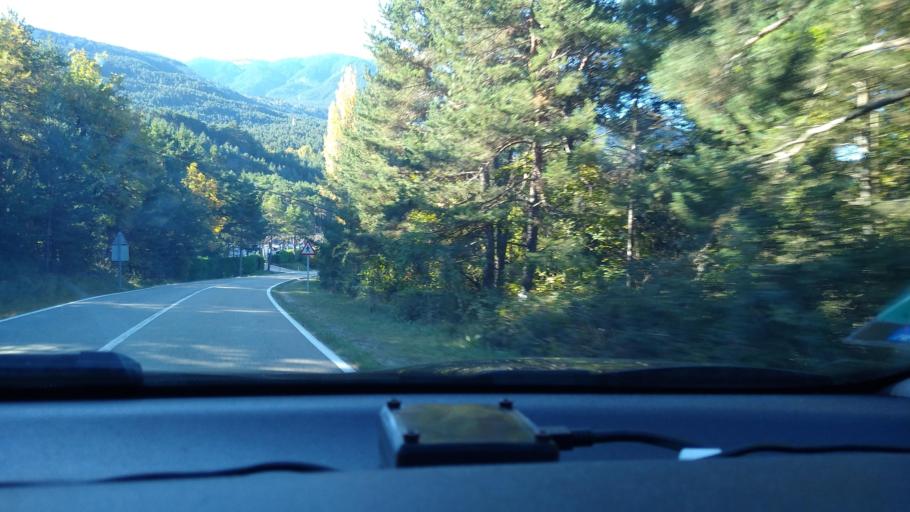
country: ES
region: Catalonia
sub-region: Provincia de Barcelona
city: Saldes
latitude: 42.2292
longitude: 1.7601
